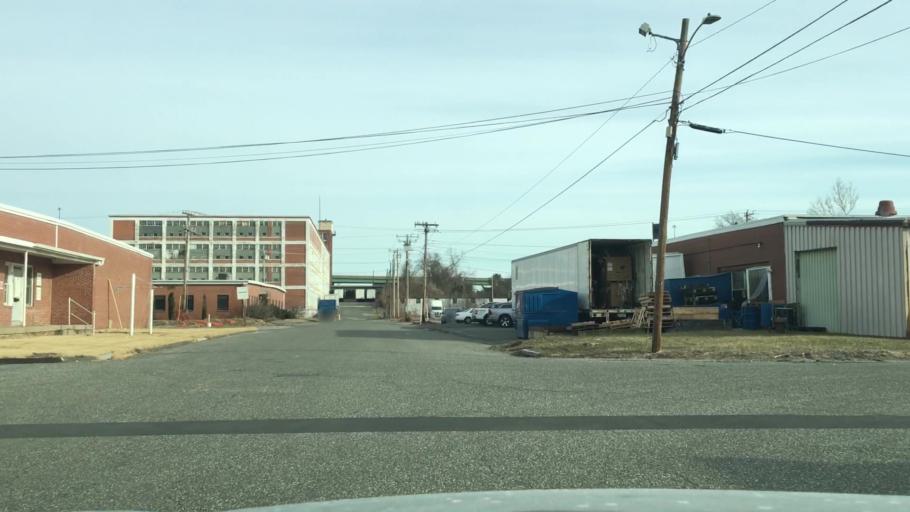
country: US
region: Massachusetts
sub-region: Hampden County
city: Holyoke
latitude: 42.1916
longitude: -72.6169
